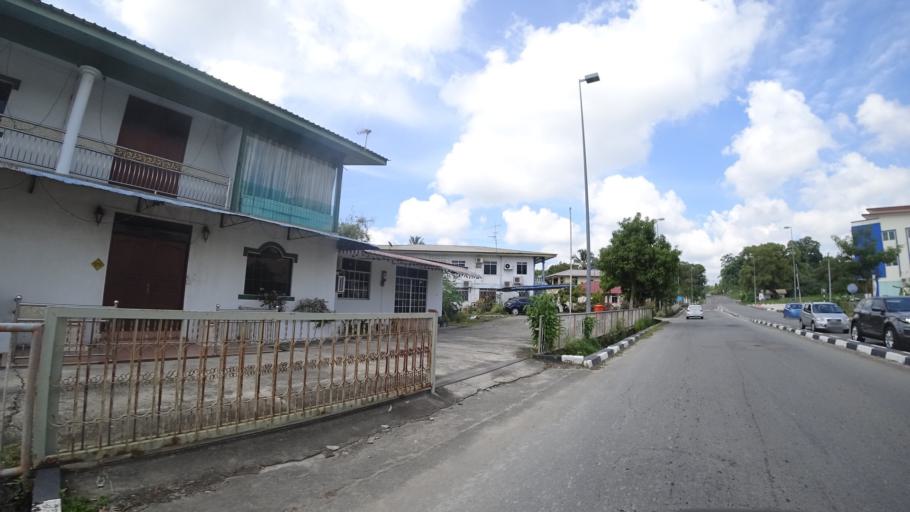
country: BN
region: Brunei and Muara
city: Bandar Seri Begawan
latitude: 4.8951
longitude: 114.9158
